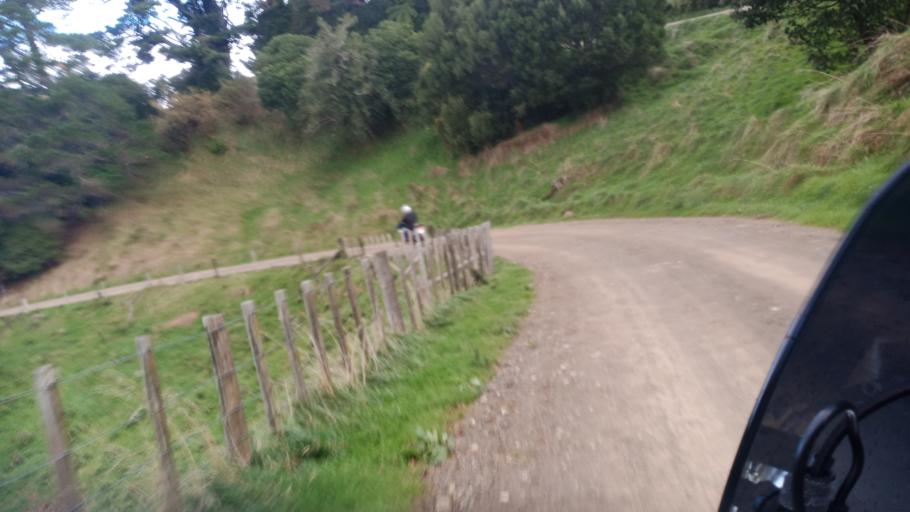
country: NZ
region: Gisborne
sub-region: Gisborne District
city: Gisborne
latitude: -38.4813
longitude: 177.6066
